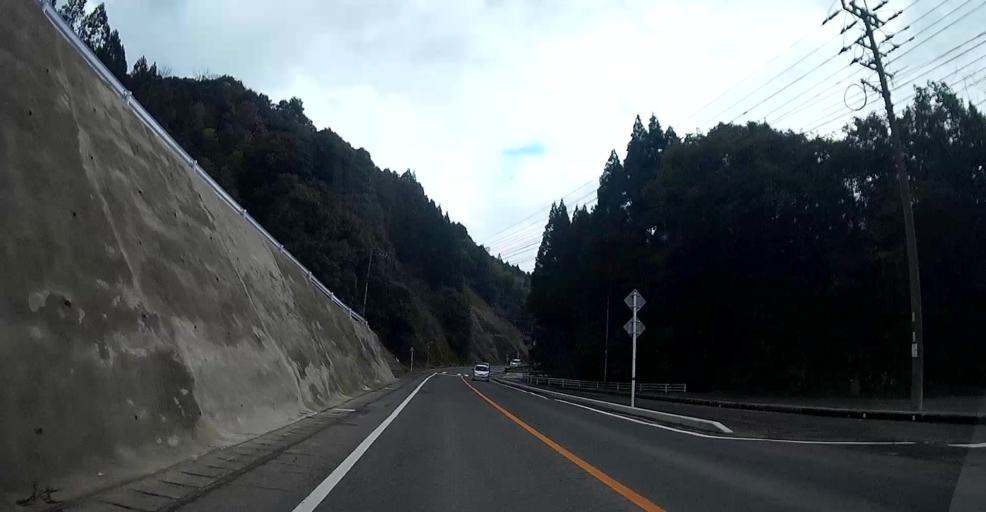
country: JP
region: Kumamoto
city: Matsubase
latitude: 32.6164
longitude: 130.8400
